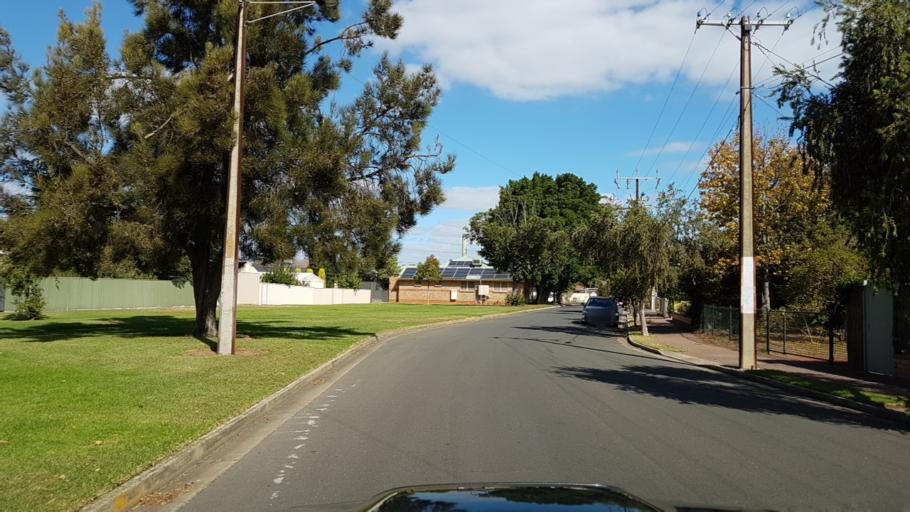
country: AU
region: South Australia
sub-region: Holdfast Bay
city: Glenelg East
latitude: -34.9726
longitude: 138.5243
